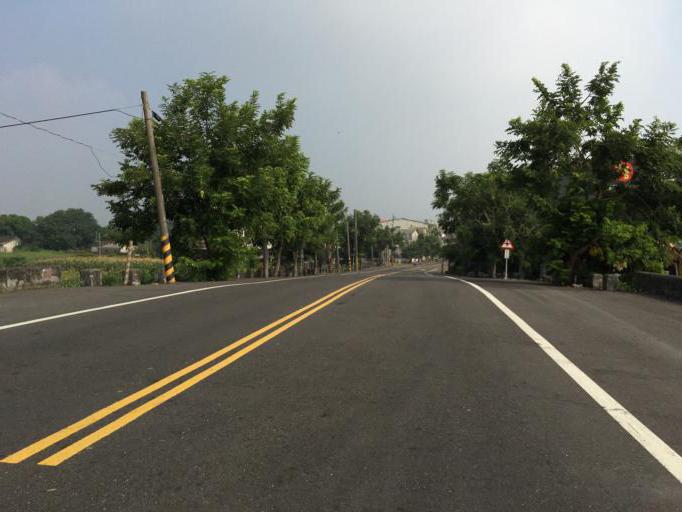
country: TW
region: Taiwan
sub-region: Chiayi
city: Taibao
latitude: 23.4838
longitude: 120.2931
